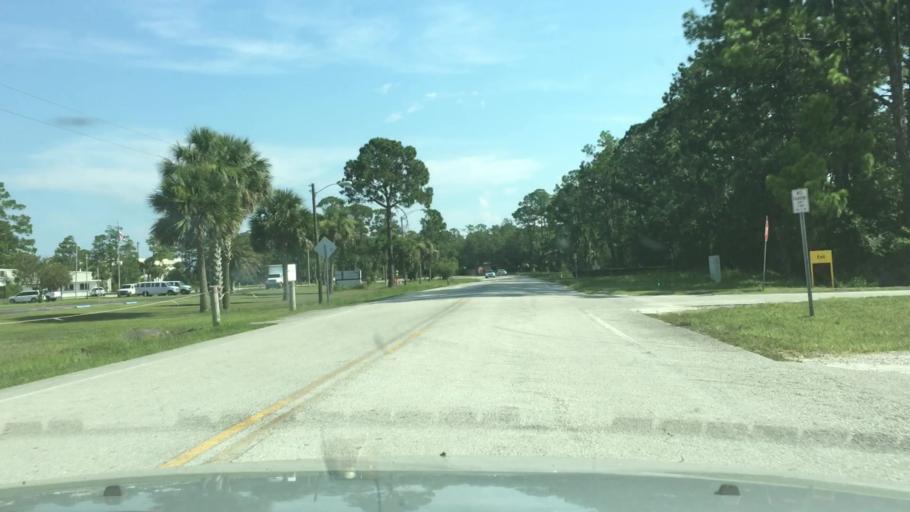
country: US
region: Florida
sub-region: Volusia County
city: Daytona Beach
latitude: 29.1923
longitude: -81.0791
